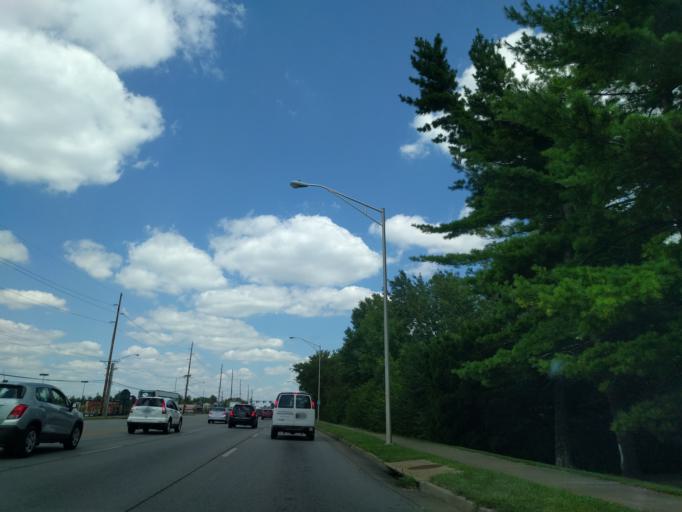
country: US
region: Kentucky
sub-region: Fayette County
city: Monticello
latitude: 37.9885
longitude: -84.5249
